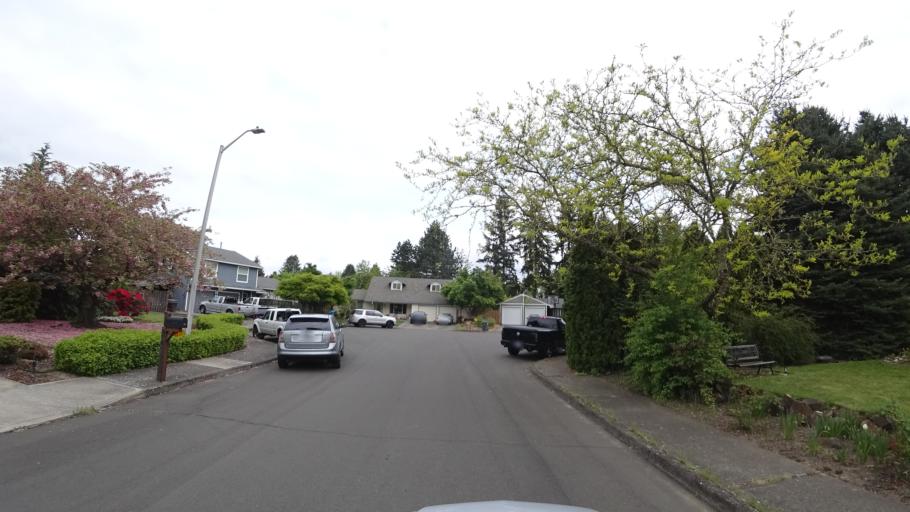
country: US
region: Oregon
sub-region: Washington County
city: Hillsboro
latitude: 45.5340
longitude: -122.9740
